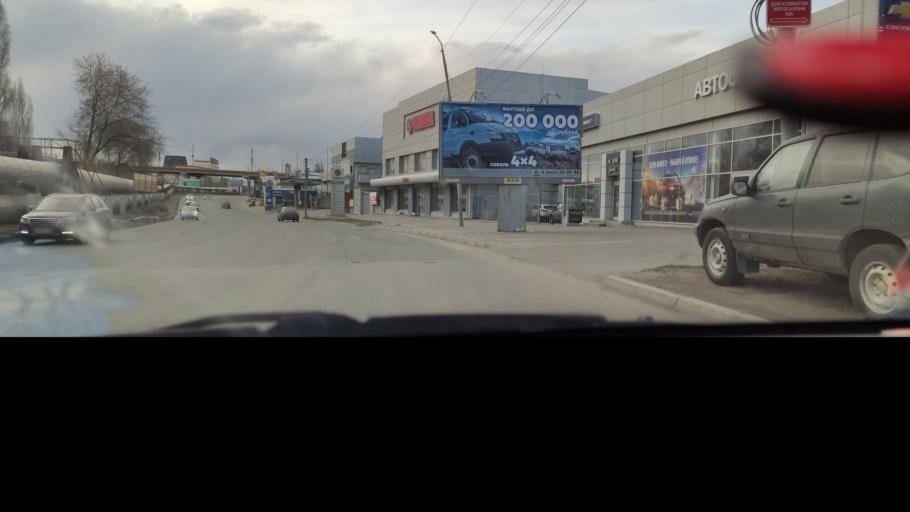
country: RU
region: Saratov
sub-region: Saratovskiy Rayon
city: Saratov
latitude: 51.5675
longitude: 45.9985
